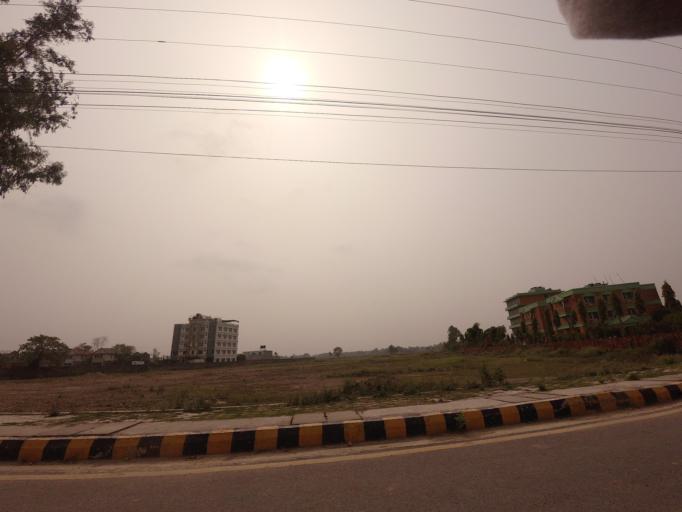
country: IN
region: Uttar Pradesh
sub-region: Maharajganj
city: Nautanwa
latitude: 27.4755
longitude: 83.2840
